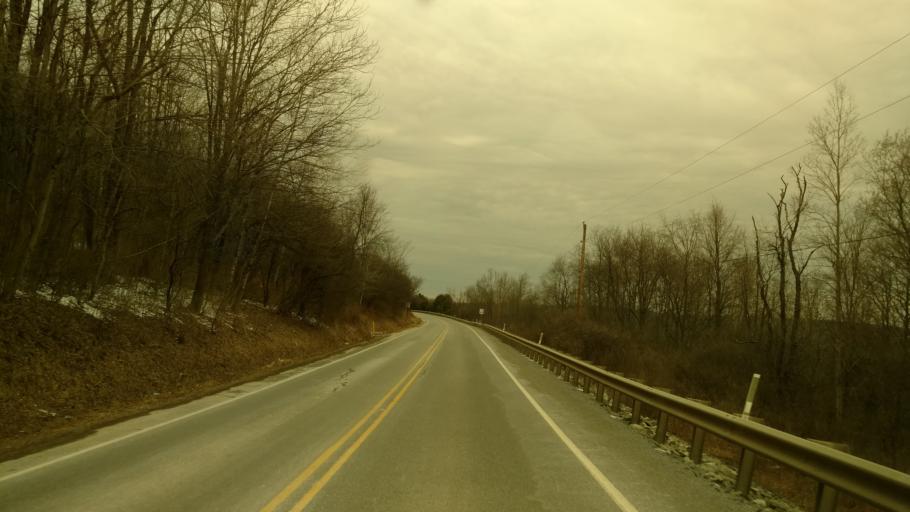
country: US
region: New York
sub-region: Allegany County
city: Wellsville
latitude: 41.9792
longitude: -77.8629
